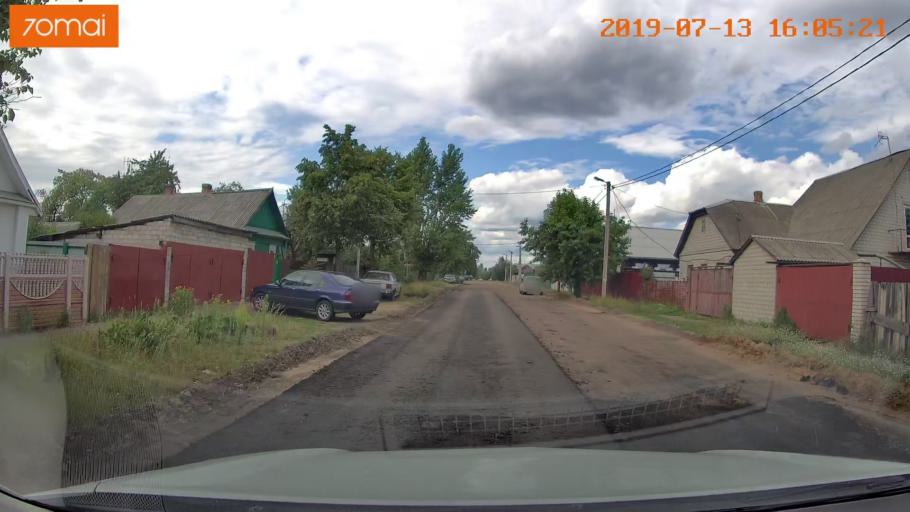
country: BY
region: Mogilev
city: Babruysk
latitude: 53.1480
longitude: 29.2053
